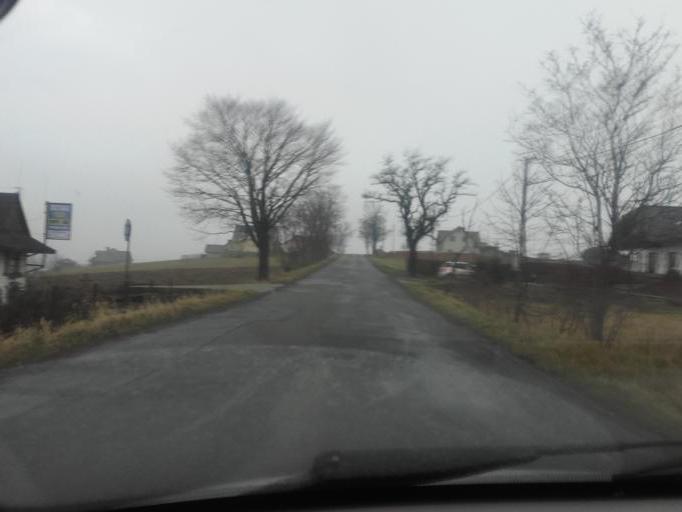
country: PL
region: Silesian Voivodeship
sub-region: Powiat cieszynski
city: Istebna
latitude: 49.5540
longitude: 18.9132
